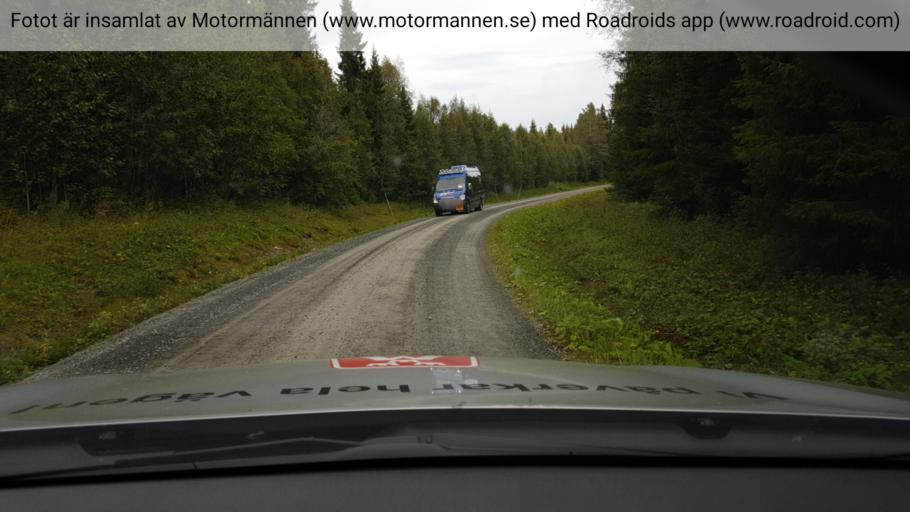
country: SE
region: Jaemtland
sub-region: Krokoms Kommun
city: Valla
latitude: 63.5301
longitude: 13.9005
